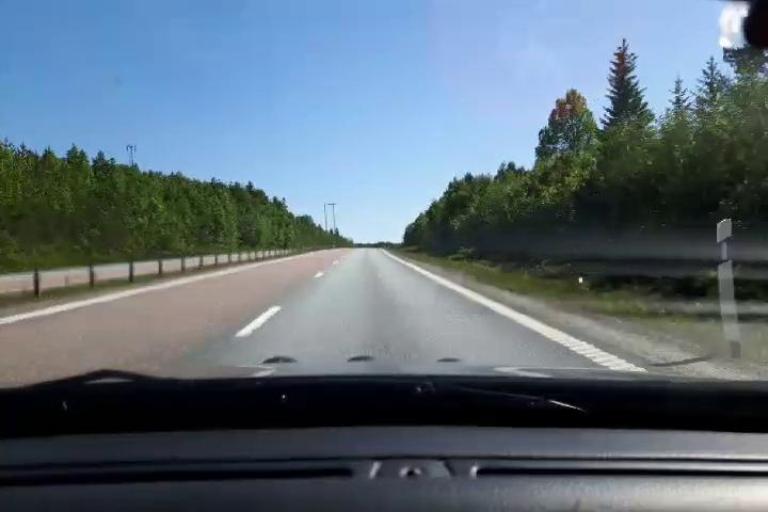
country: SE
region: Gaevleborg
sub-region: Hudiksvalls Kommun
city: Iggesund
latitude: 61.5087
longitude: 16.9857
